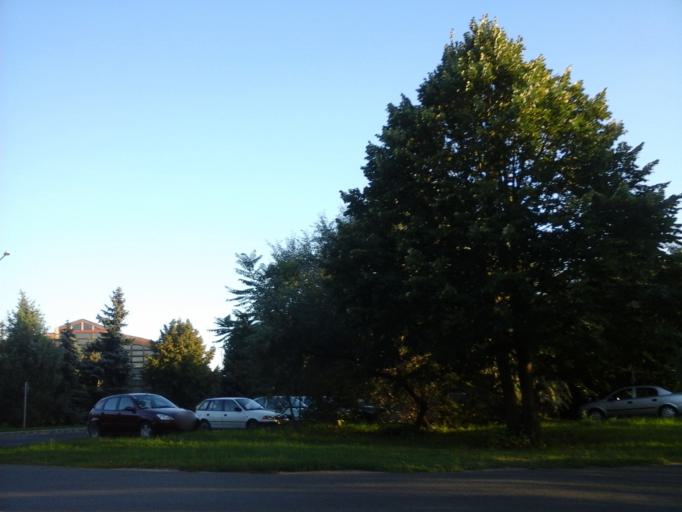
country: HU
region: Hajdu-Bihar
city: Hajduszoboszlo
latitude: 47.4579
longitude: 21.3962
